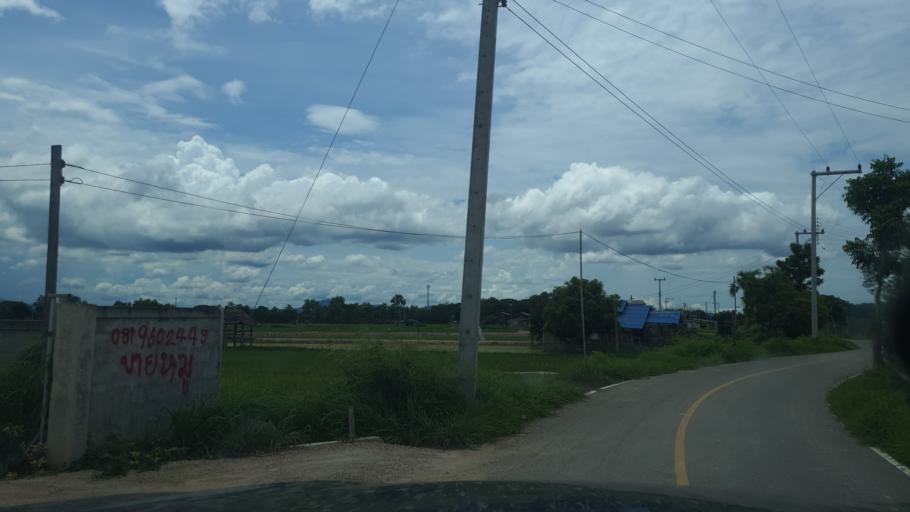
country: TH
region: Lampang
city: Sop Prap
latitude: 17.8749
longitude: 99.3844
